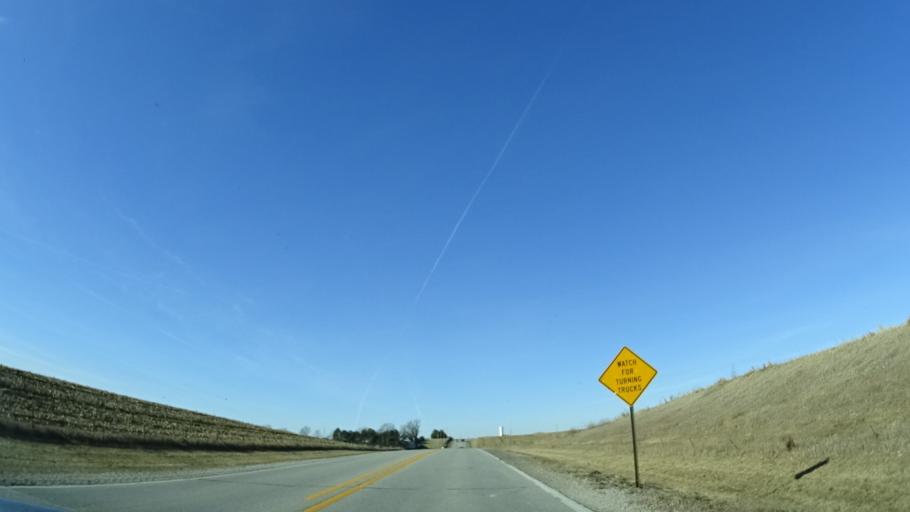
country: US
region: Nebraska
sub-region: Sarpy County
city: Springfield
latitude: 41.0889
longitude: -96.0965
